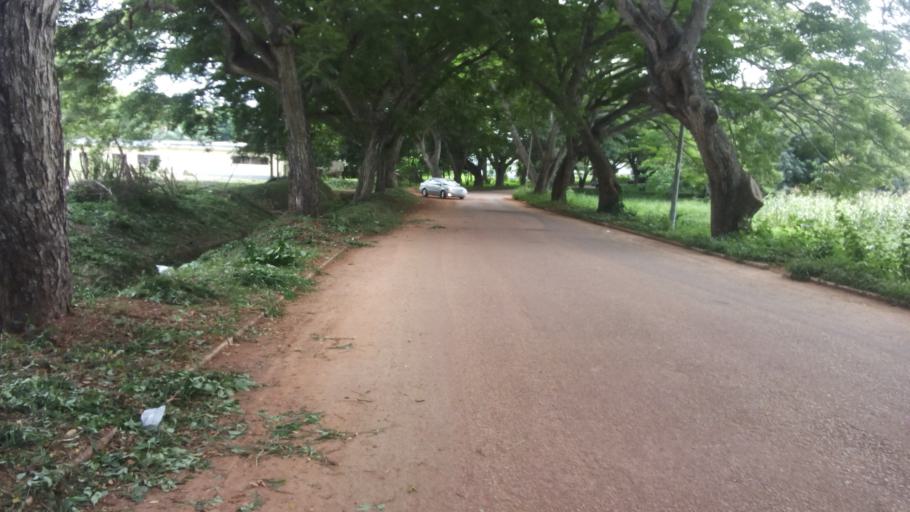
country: GH
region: Central
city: Cape Coast
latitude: 5.1256
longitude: -1.2864
